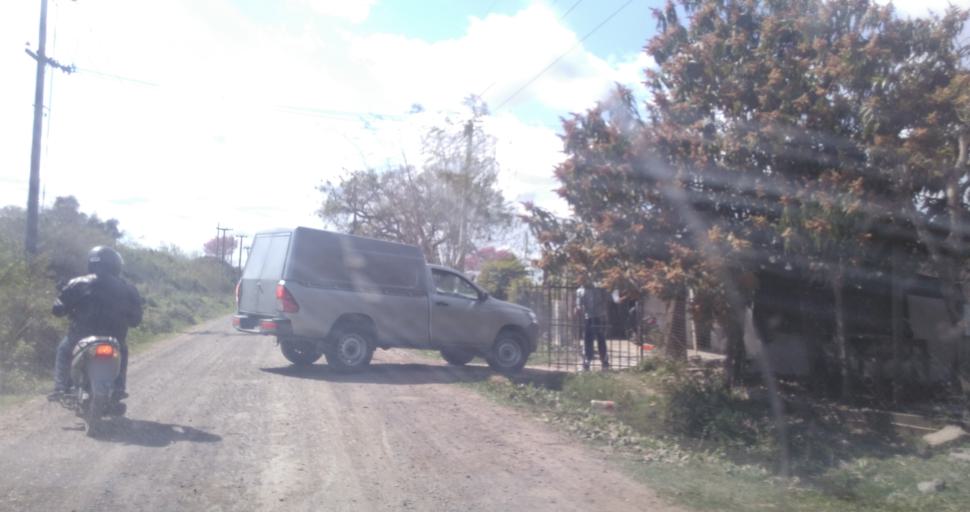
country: AR
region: Chaco
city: Fontana
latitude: -27.4298
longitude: -59.0219
